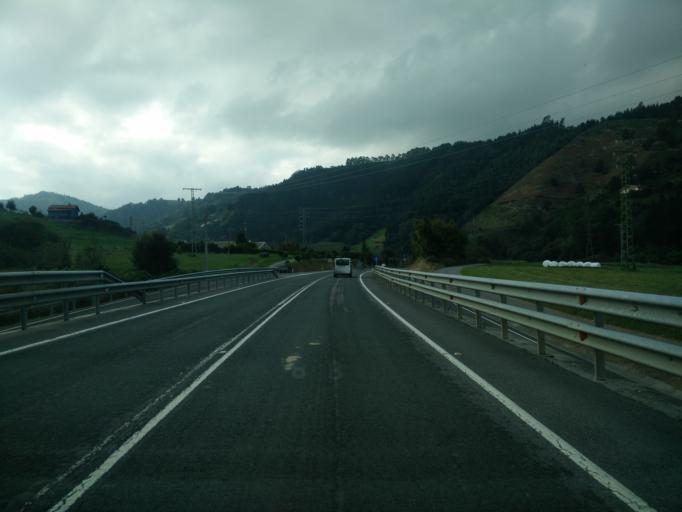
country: ES
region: Basque Country
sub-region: Bizkaia
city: Ondarroa
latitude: 43.3191
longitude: -2.4382
